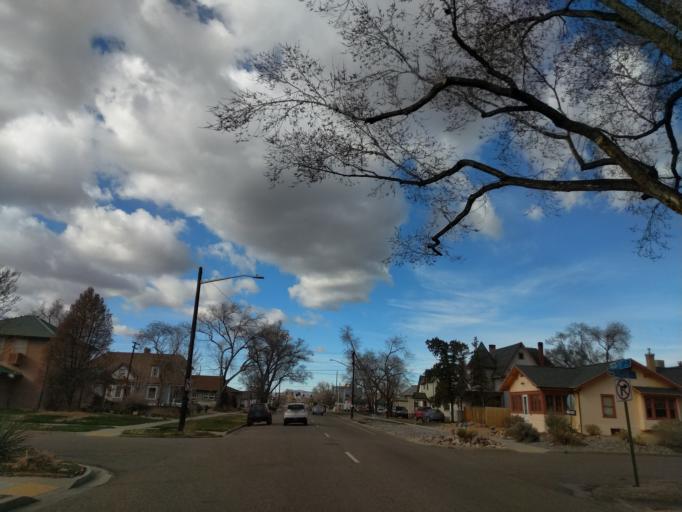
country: US
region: Colorado
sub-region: Mesa County
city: Grand Junction
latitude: 39.0752
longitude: -108.5645
